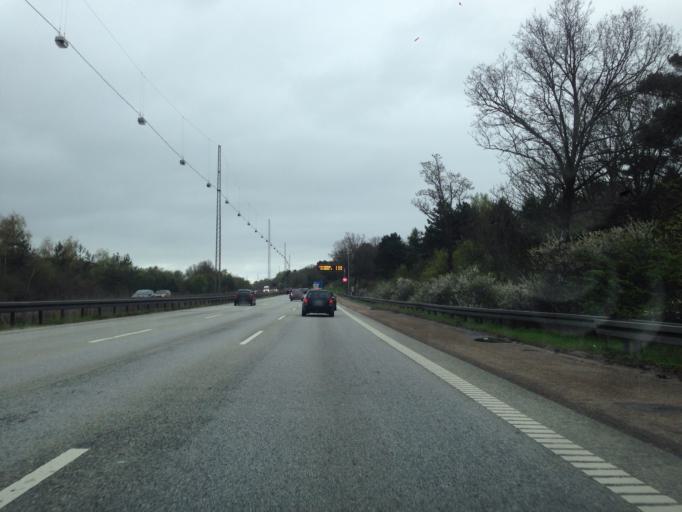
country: DK
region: Capital Region
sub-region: Rudersdal Kommune
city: Trorod
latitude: 55.8033
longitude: 12.5334
